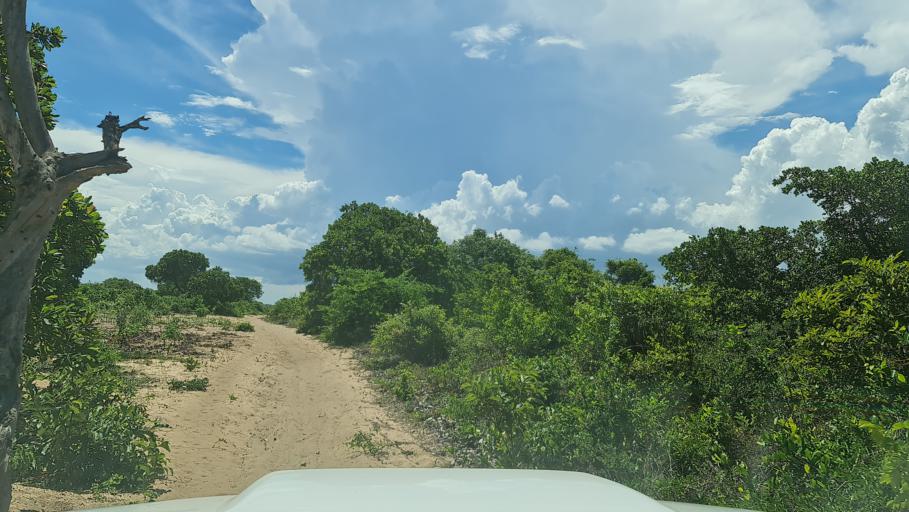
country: MZ
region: Nampula
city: Antonio Enes
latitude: -15.7069
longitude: 40.2577
